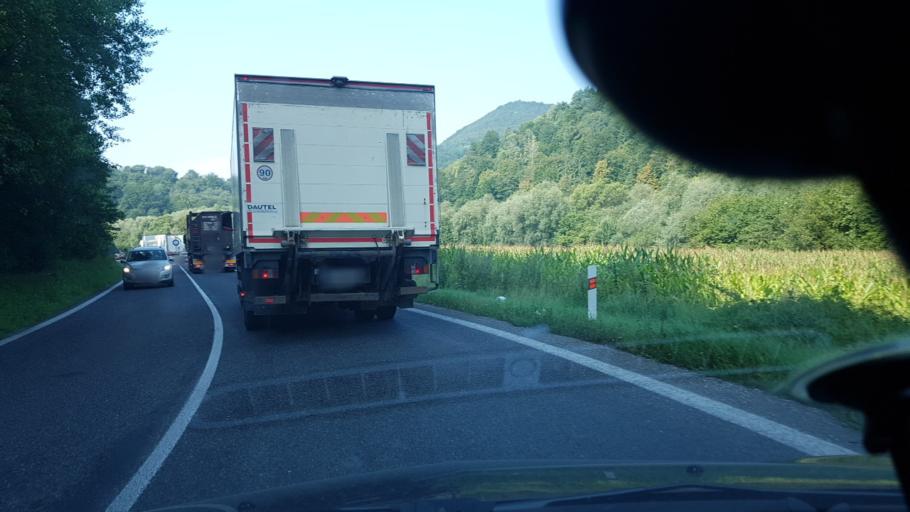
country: SK
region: Zilinsky
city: Tvrdosin
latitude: 49.2805
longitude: 19.4642
